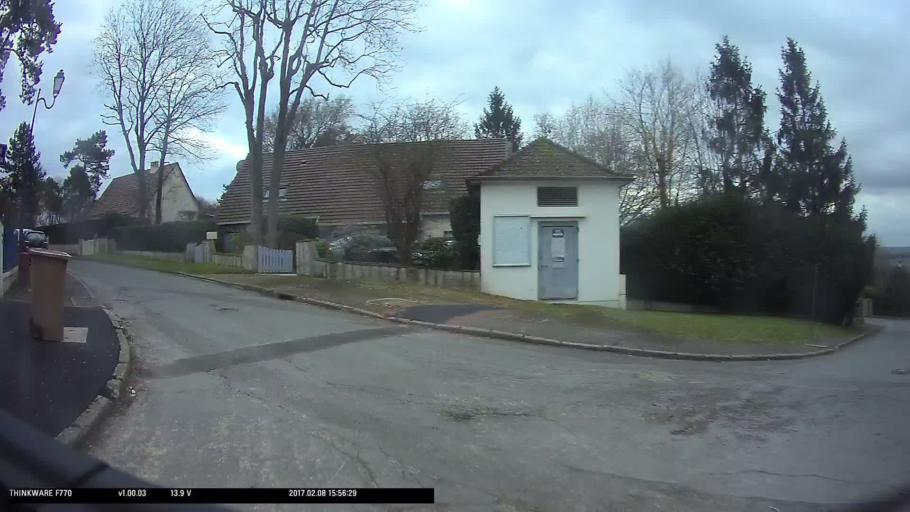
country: FR
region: Ile-de-France
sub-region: Departement du Val-d'Oise
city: Vigny
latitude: 49.0789
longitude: 1.9326
